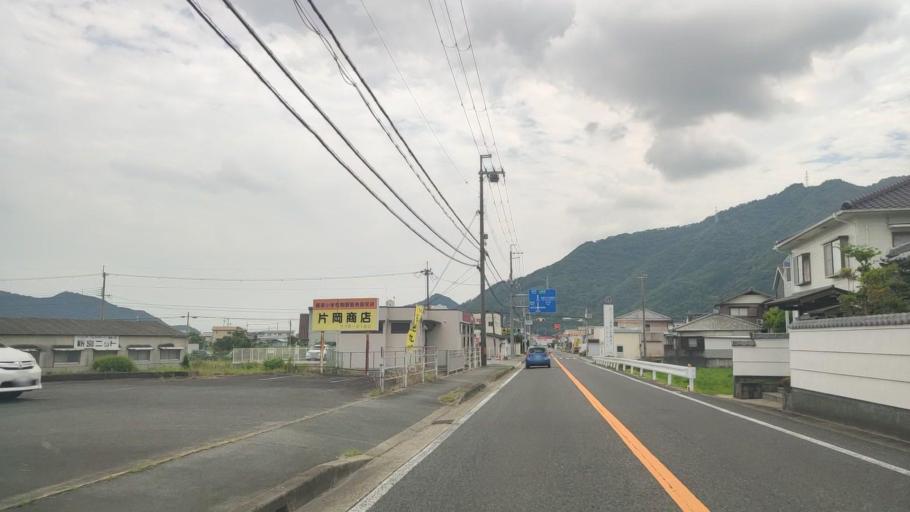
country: JP
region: Hyogo
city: Tatsunocho-tominaga
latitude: 34.8983
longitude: 134.5469
